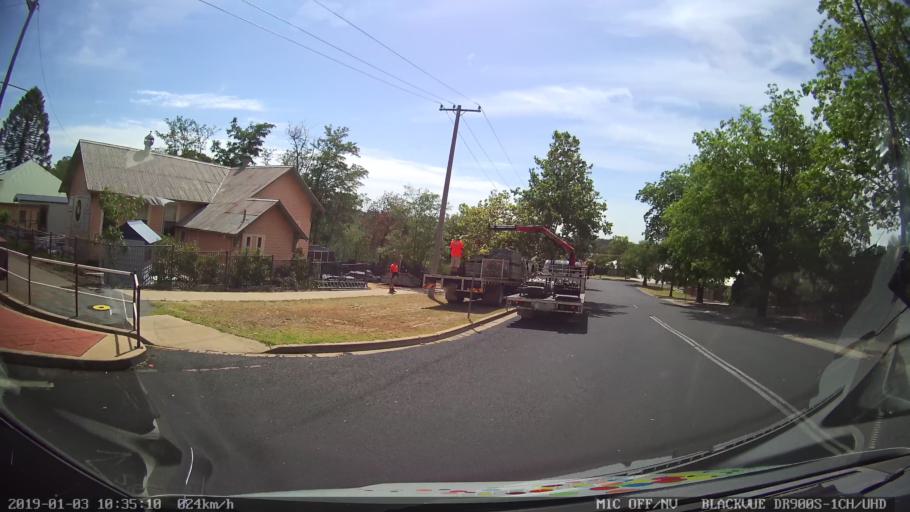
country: AU
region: New South Wales
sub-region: Young
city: Young
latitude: -34.3174
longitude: 148.2936
